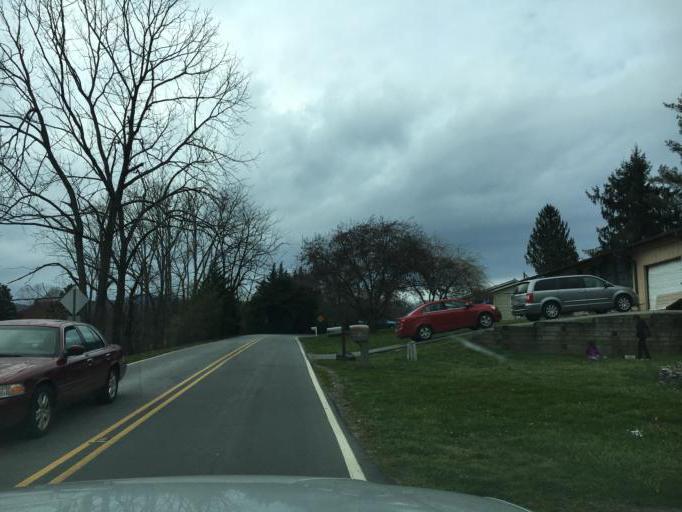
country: US
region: North Carolina
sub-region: Transylvania County
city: Brevard
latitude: 35.2404
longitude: -82.7208
